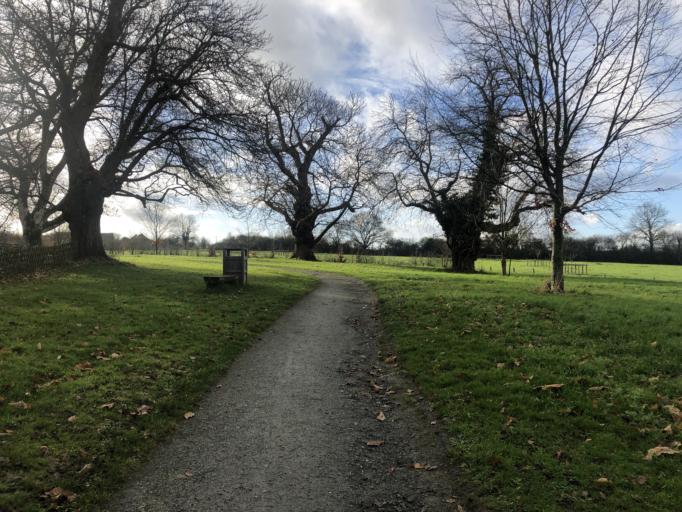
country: FR
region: Pays de la Loire
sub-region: Departement de Maine-et-Loire
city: Le Plessis-Mace
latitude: 47.5450
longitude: -0.6766
